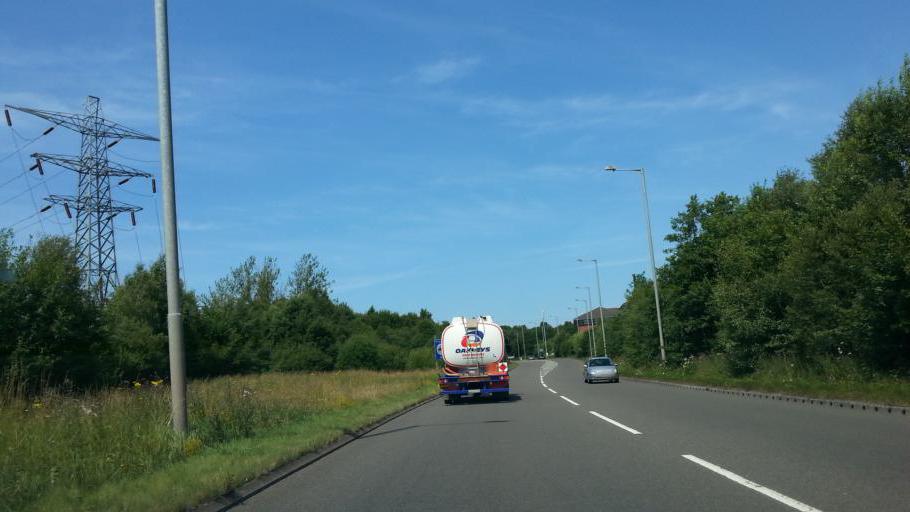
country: GB
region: England
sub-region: Staffordshire
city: Norton Canes
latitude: 52.6815
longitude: -1.9525
